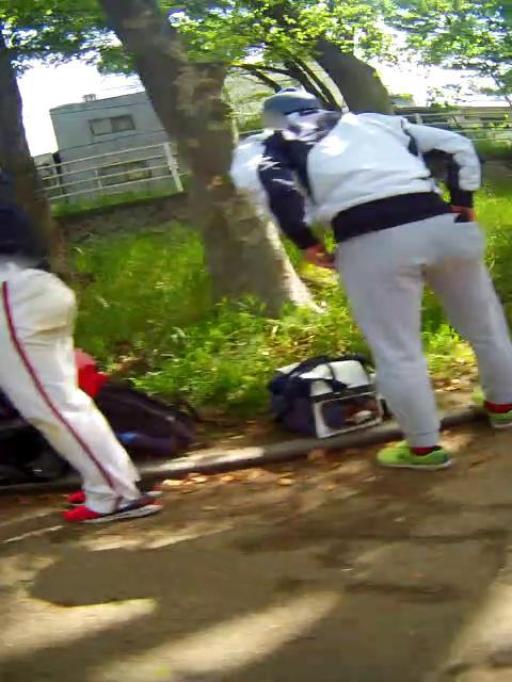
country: JP
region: Osaka
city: Osaka-shi
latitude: 34.7031
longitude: 135.5210
